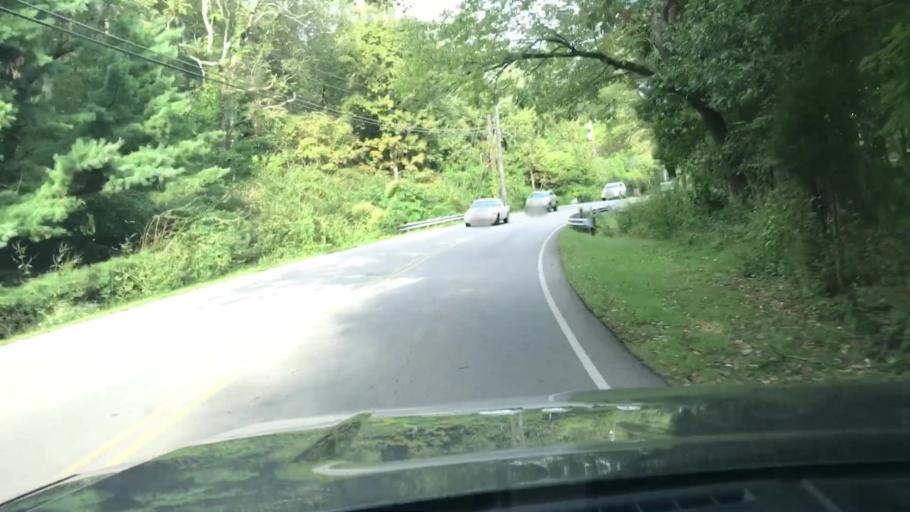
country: US
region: Tennessee
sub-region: Davidson County
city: Forest Hills
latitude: 36.0707
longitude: -86.8293
